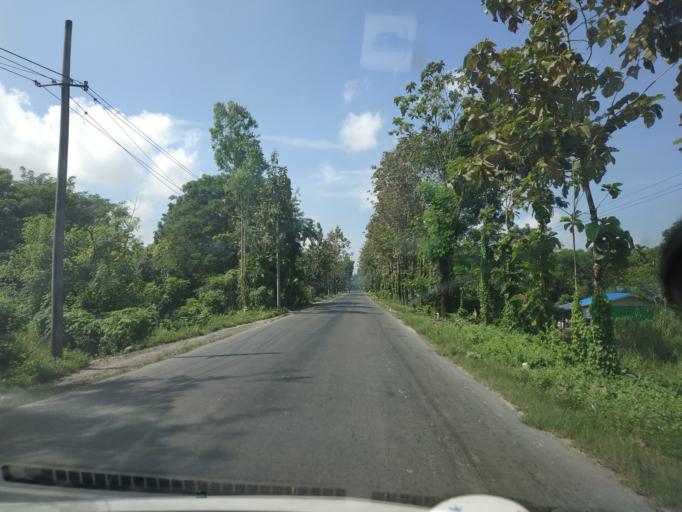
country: MM
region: Ayeyarwady
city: Nyaungdon
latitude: 17.0427
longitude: 95.5417
